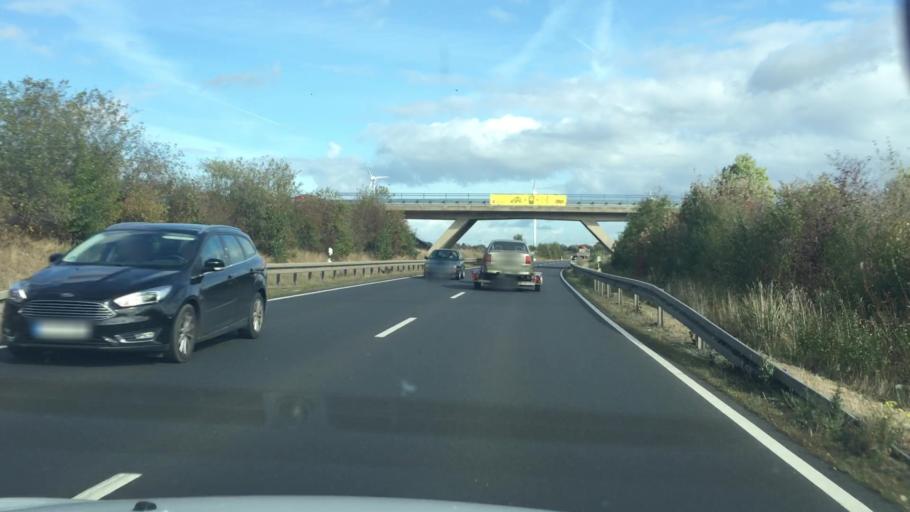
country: DE
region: Lower Saxony
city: Diepholz
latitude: 52.6261
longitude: 8.3789
